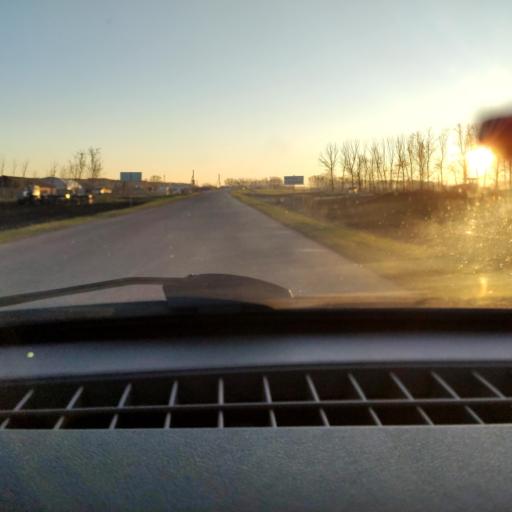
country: RU
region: Bashkortostan
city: Avdon
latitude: 54.5483
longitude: 55.6562
